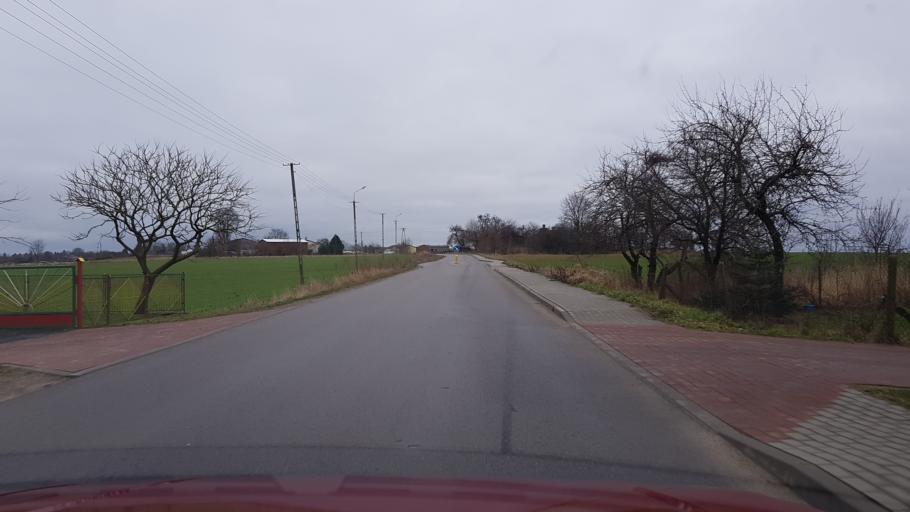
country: PL
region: West Pomeranian Voivodeship
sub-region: Powiat koszalinski
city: Mielno
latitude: 54.1690
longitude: 16.0263
